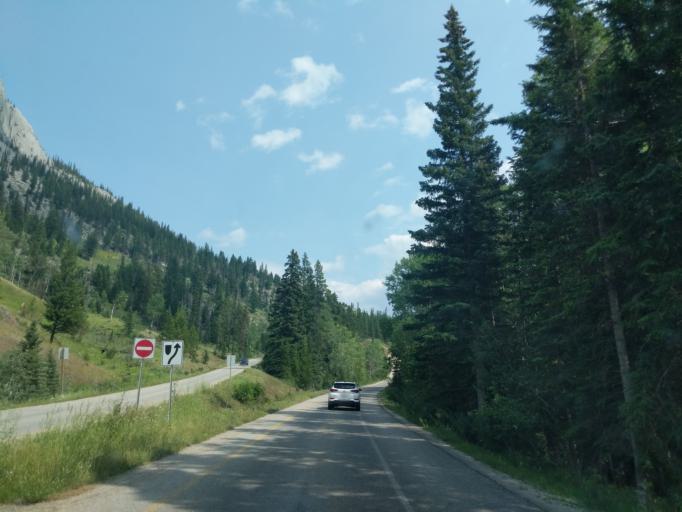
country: CA
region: Alberta
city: Banff
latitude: 51.1718
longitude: -115.7047
